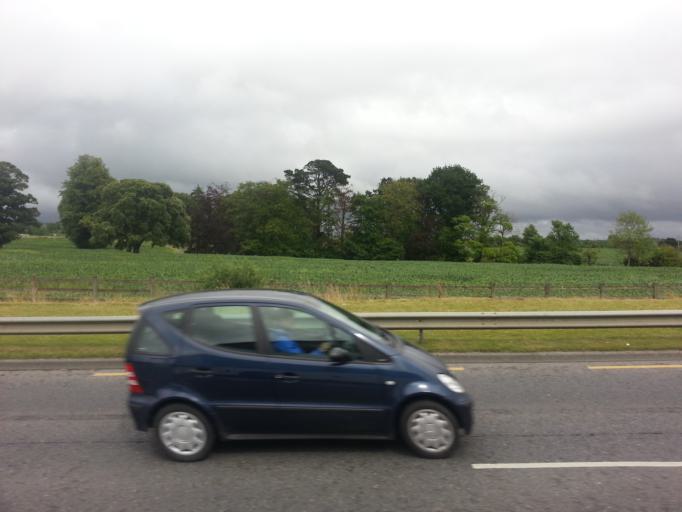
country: IE
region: Leinster
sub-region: Kilkenny
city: Kilkenny
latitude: 52.6570
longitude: -7.2256
